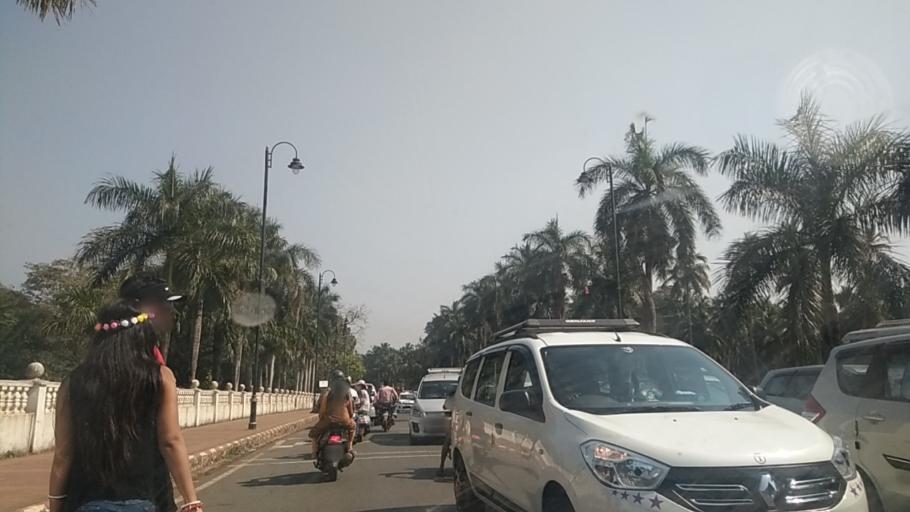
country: IN
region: Goa
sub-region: North Goa
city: Jua
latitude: 15.5016
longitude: 73.9116
